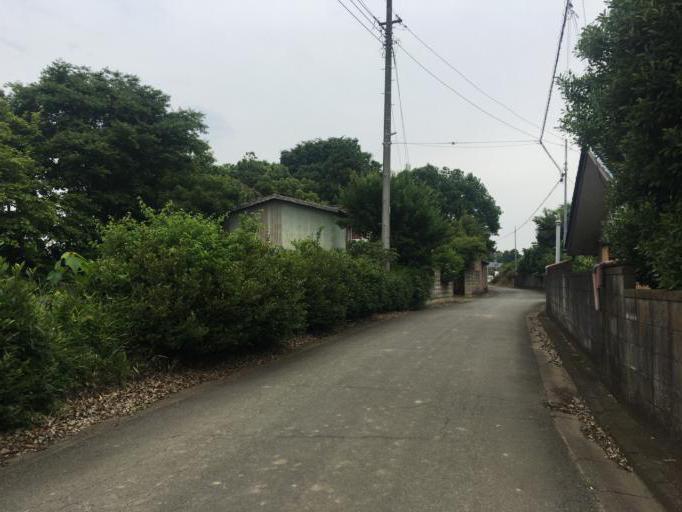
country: JP
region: Saitama
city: Sakado
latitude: 36.0158
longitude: 139.4378
